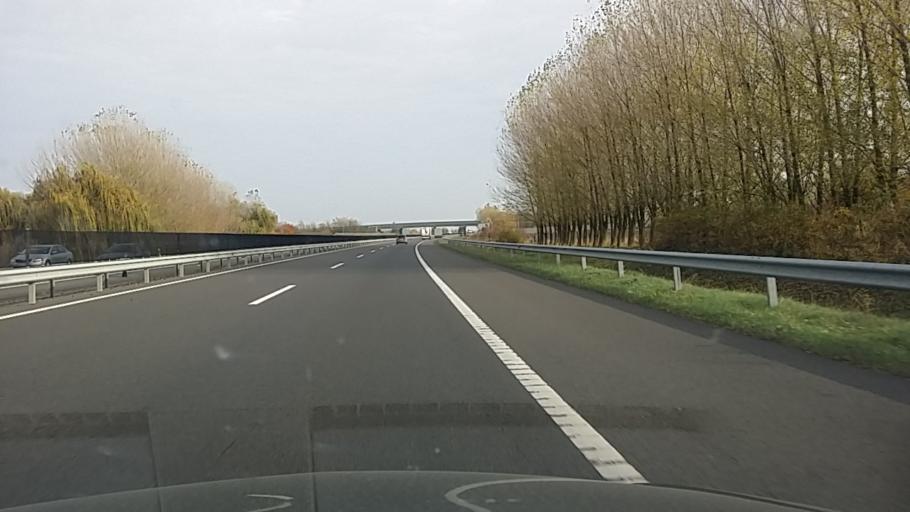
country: HU
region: Szabolcs-Szatmar-Bereg
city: Nyiregyhaza
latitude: 47.9020
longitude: 21.6618
